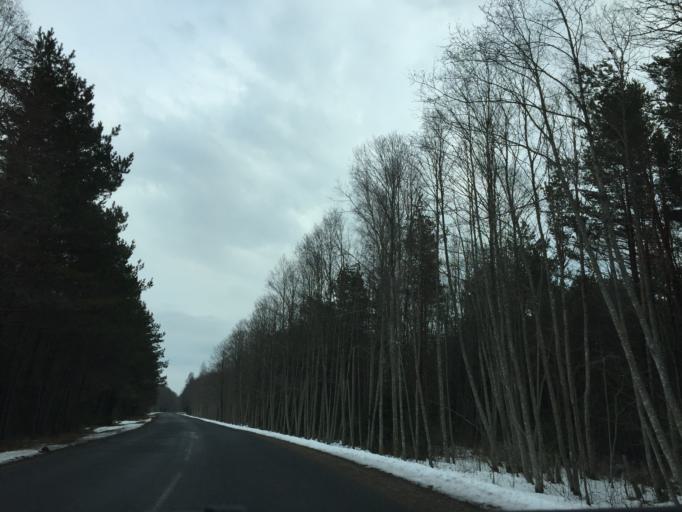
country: EE
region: Saare
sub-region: Kuressaare linn
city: Kuressaare
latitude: 58.4161
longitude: 22.0797
